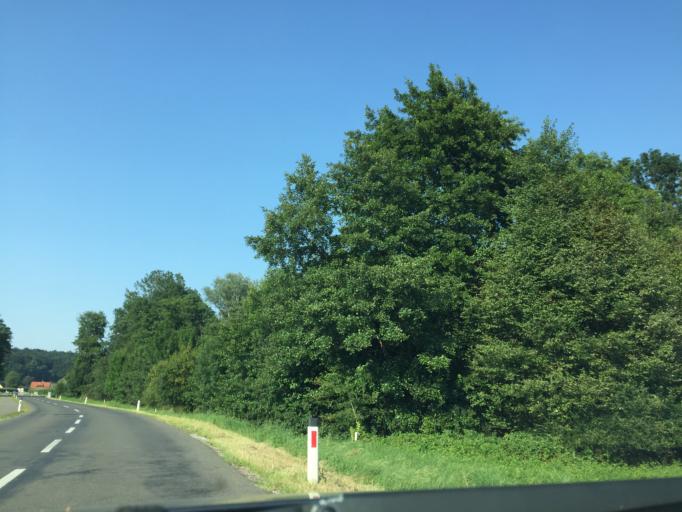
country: AT
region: Styria
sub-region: Politischer Bezirk Suedoststeiermark
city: Deutsch Goritz
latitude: 46.7551
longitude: 15.8382
